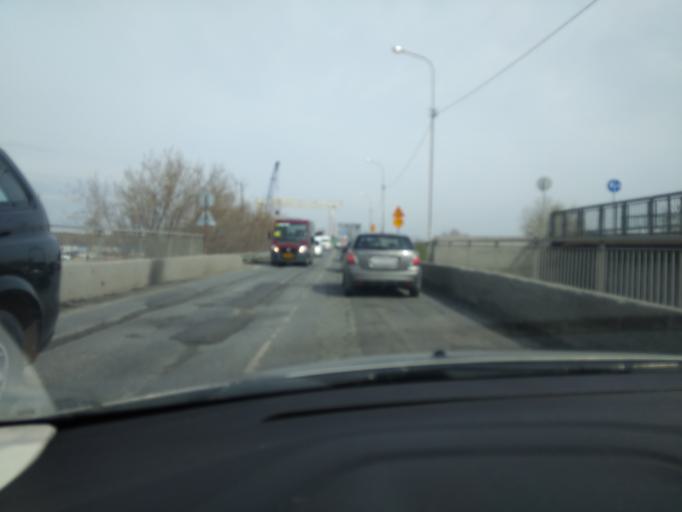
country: RU
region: Tjumen
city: Melioratorov
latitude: 57.1555
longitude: 65.5983
